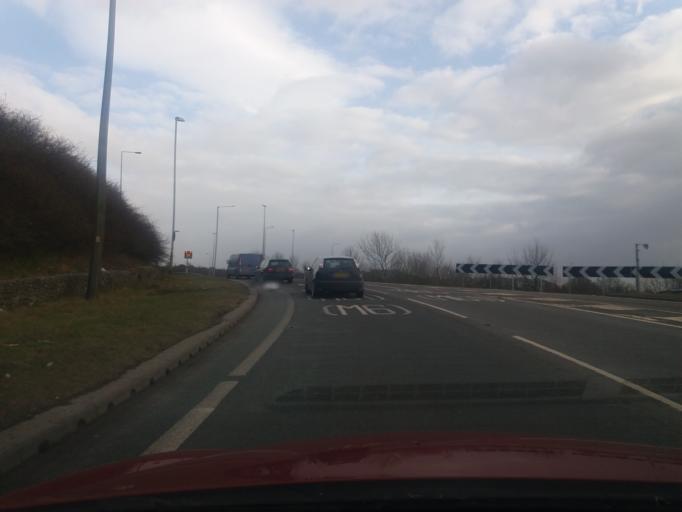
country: GB
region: England
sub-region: Lancashire
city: Clayton-le-Woods
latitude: 53.7188
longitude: -2.6745
